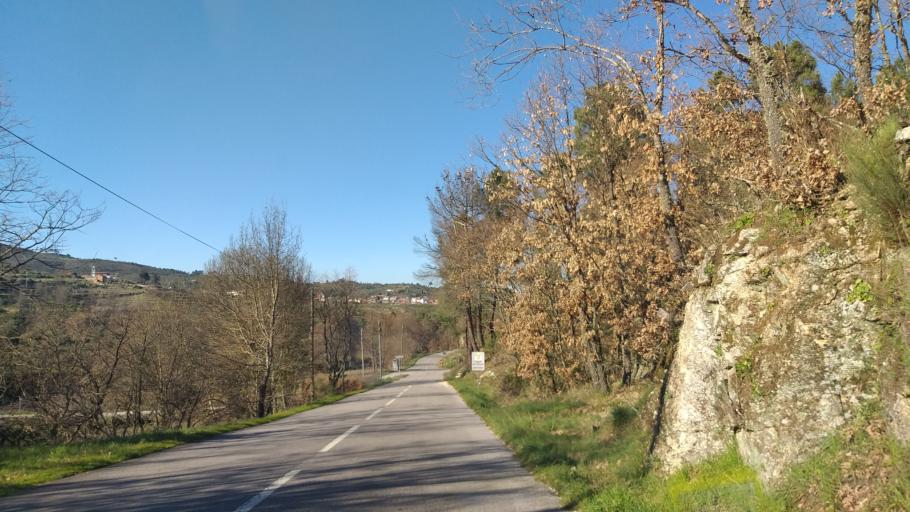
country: PT
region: Guarda
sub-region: Celorico da Beira
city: Celorico da Beira
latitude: 40.5951
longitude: -7.3629
